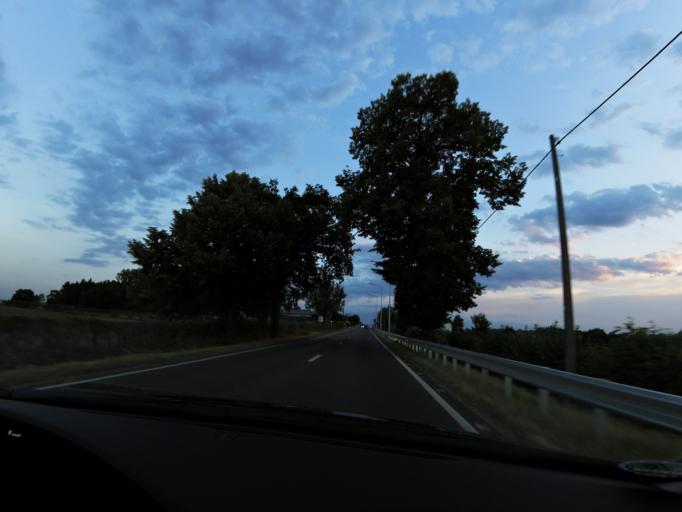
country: BE
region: Wallonia
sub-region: Province de Liege
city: Welkenraedt
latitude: 50.6868
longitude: 5.9574
